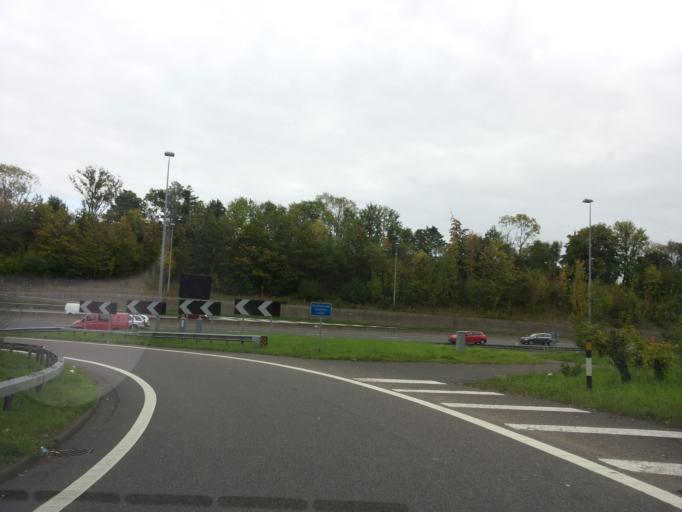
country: GB
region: England
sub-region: Hertfordshire
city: Chorleywood
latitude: 51.6546
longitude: -0.4968
